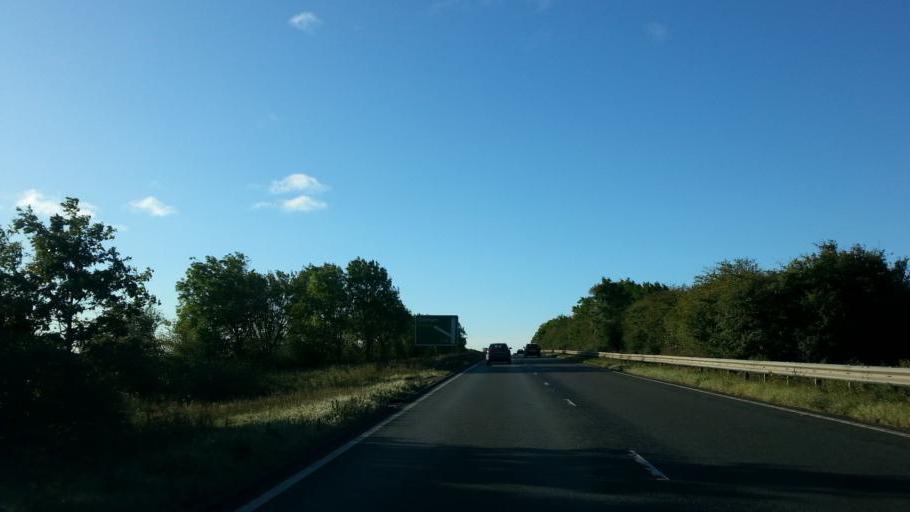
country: GB
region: England
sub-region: District of Rutland
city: Greetham
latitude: 52.7446
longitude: -0.6033
